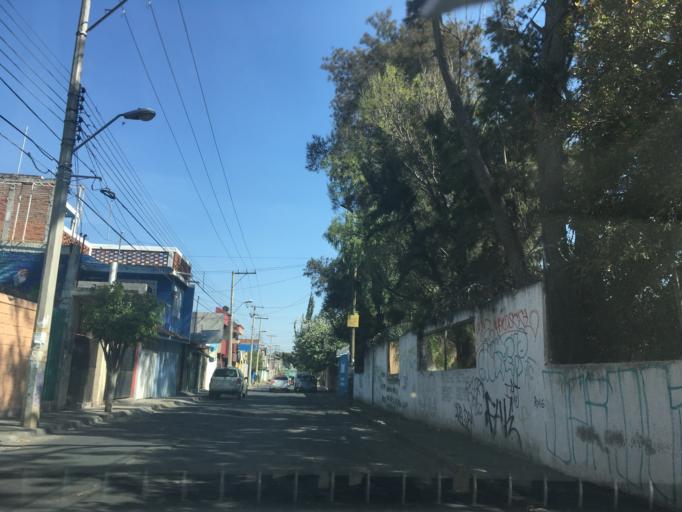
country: MX
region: Michoacan
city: Morelia
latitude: 19.6862
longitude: -101.2018
